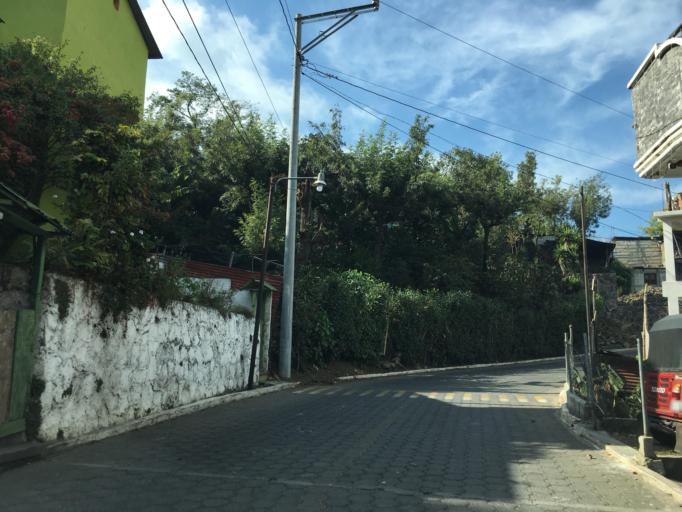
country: GT
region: Solola
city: San Antonio Palopo
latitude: 14.6601
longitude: -91.1615
